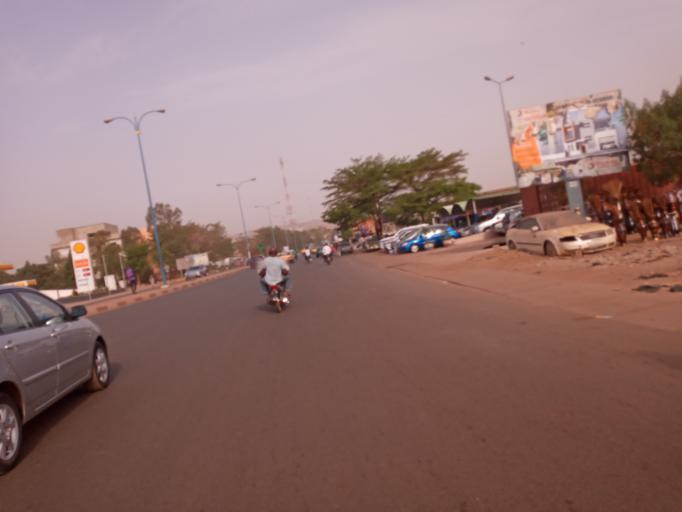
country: ML
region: Bamako
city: Bamako
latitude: 12.6373
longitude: -8.0171
